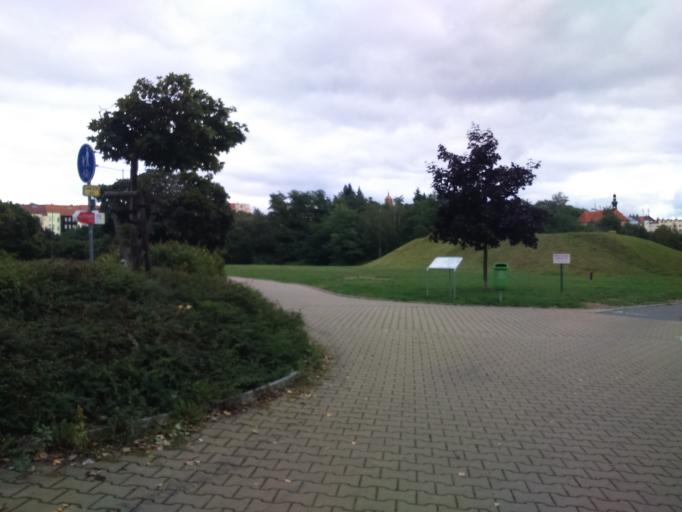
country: CZ
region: Plzensky
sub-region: Okres Plzen-Mesto
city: Pilsen
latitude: 49.7408
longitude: 13.3823
